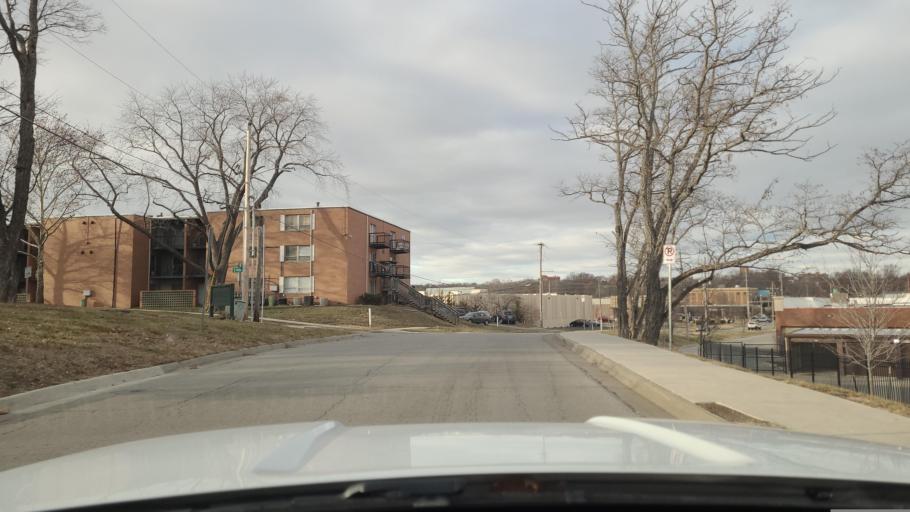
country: US
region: Kansas
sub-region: Douglas County
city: Lawrence
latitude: 38.9407
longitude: -95.2554
